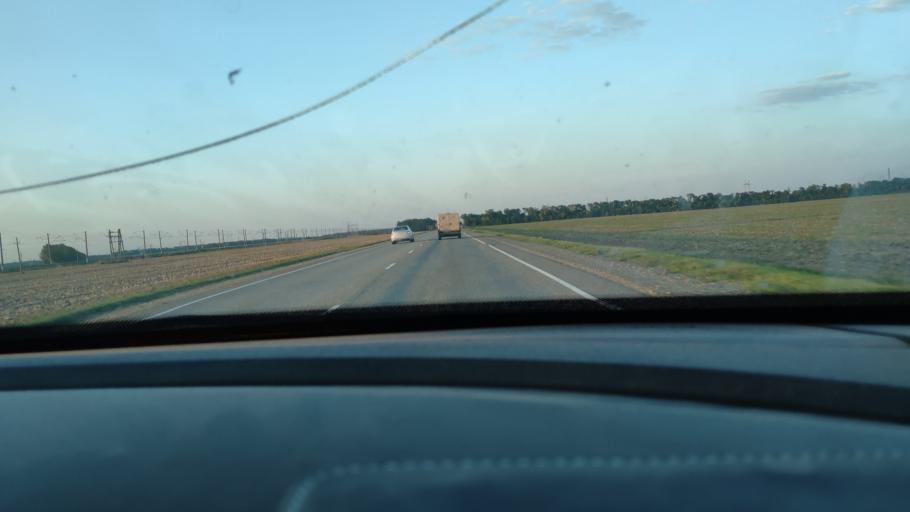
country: RU
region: Krasnodarskiy
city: Novominskaya
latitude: 46.3874
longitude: 38.9874
